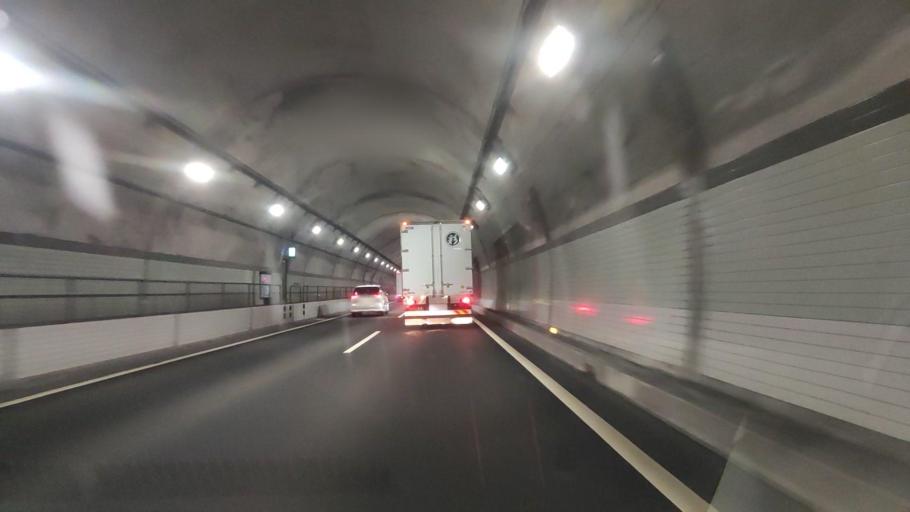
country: JP
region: Tokyo
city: Itsukaichi
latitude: 35.6719
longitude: 139.2509
